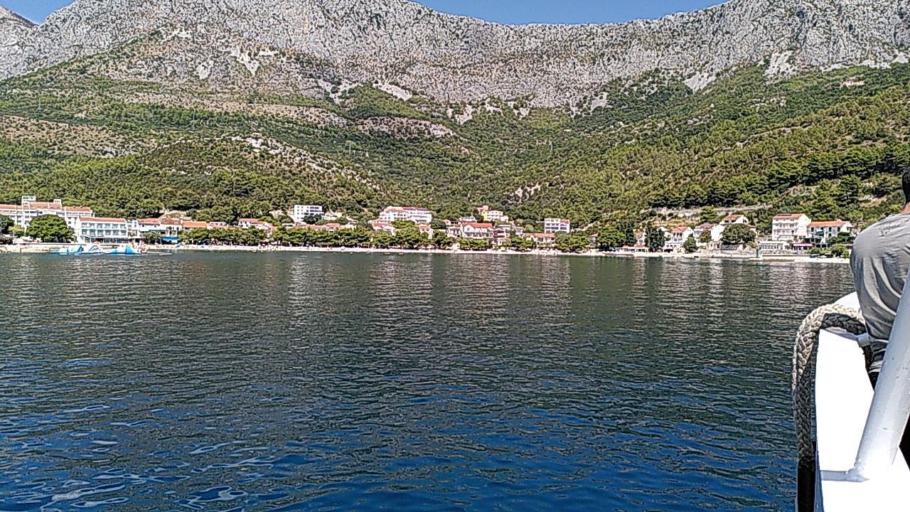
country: HR
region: Splitsko-Dalmatinska
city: Vrgorac
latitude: 43.1522
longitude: 17.2463
